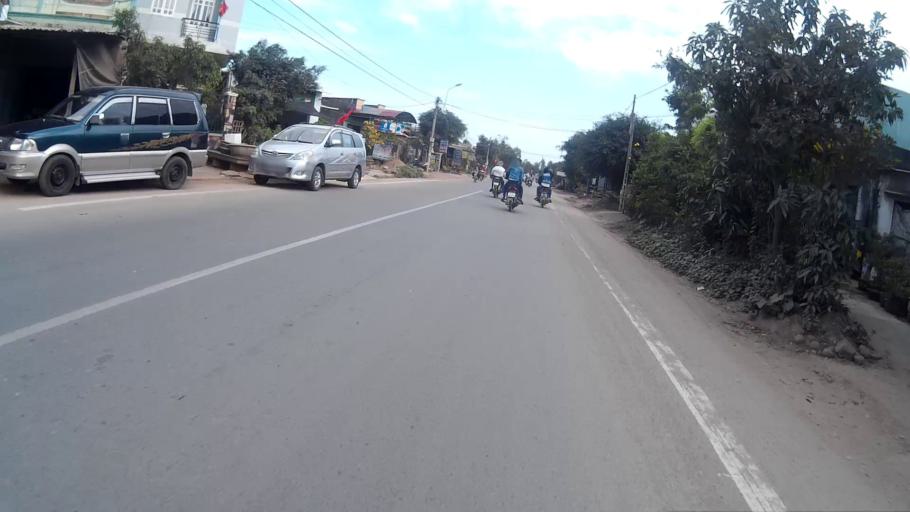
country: VN
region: Binh Dinh
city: An Nhon
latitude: 13.8626
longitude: 109.1332
